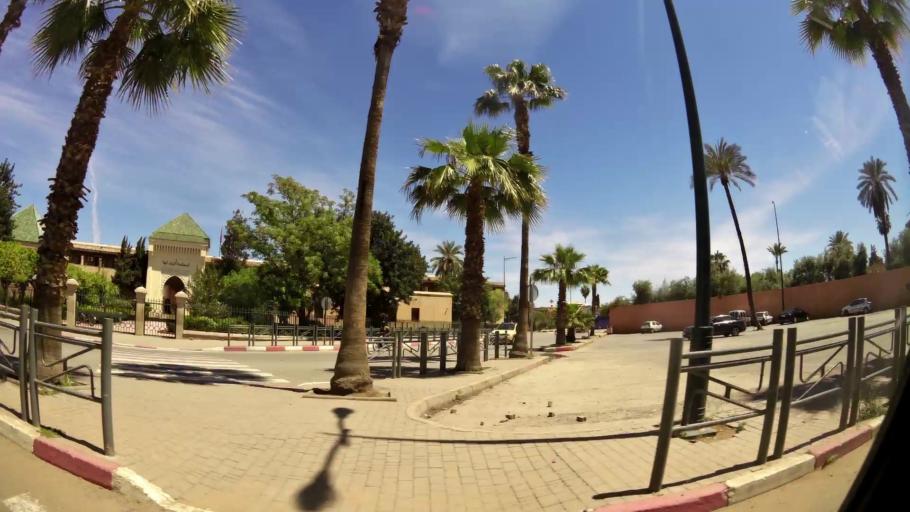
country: MA
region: Marrakech-Tensift-Al Haouz
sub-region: Marrakech
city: Marrakesh
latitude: 31.6319
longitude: -7.9996
